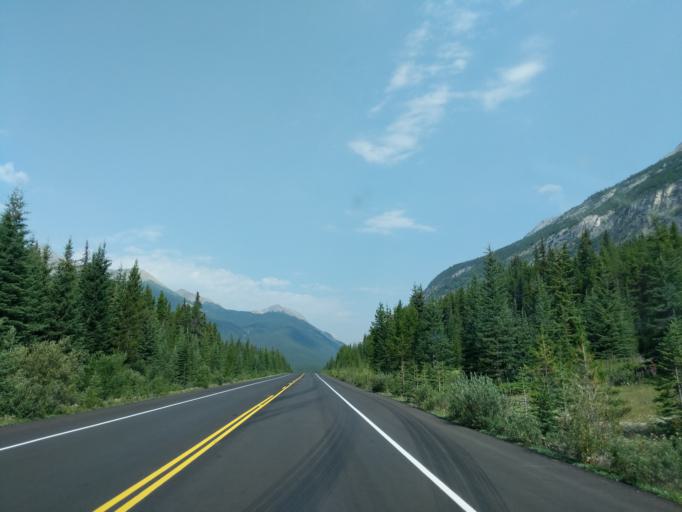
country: CA
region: British Columbia
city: Golden
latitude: 52.0976
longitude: -116.9538
